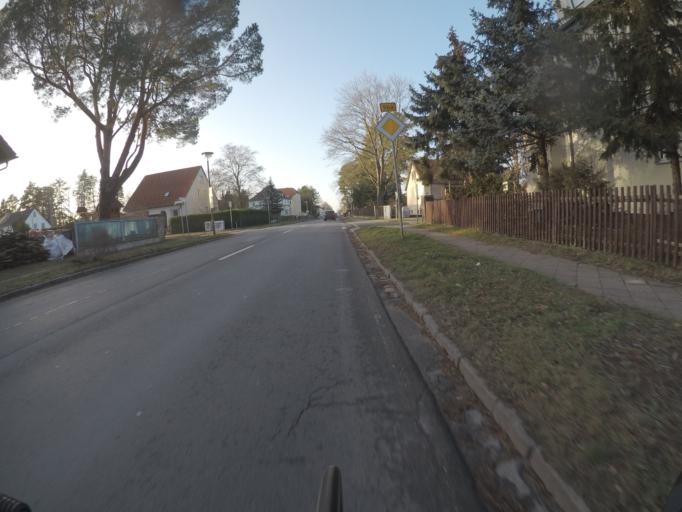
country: DE
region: Brandenburg
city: Birkenwerder
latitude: 52.6850
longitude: 13.2952
